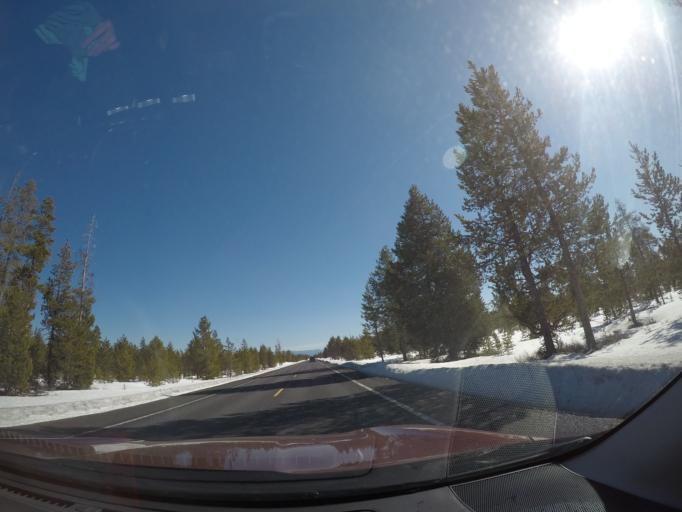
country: US
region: Oregon
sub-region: Deschutes County
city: Three Rivers
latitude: 43.8857
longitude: -121.5773
